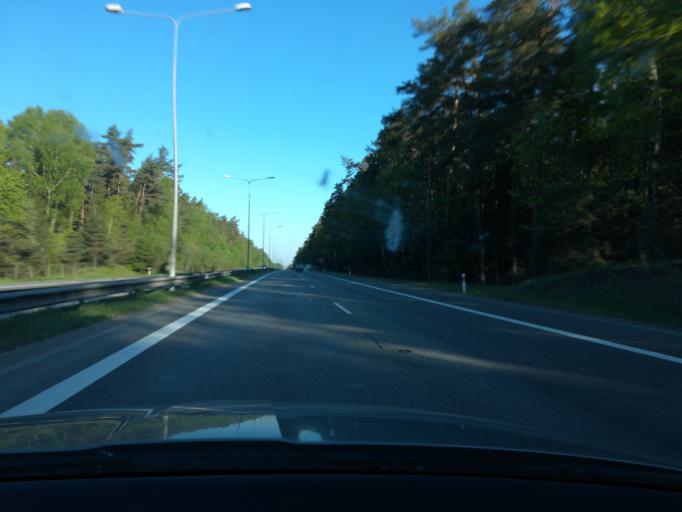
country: LT
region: Kauno apskritis
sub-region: Kauno rajonas
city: Karmelava
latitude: 54.8903
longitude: 24.1662
